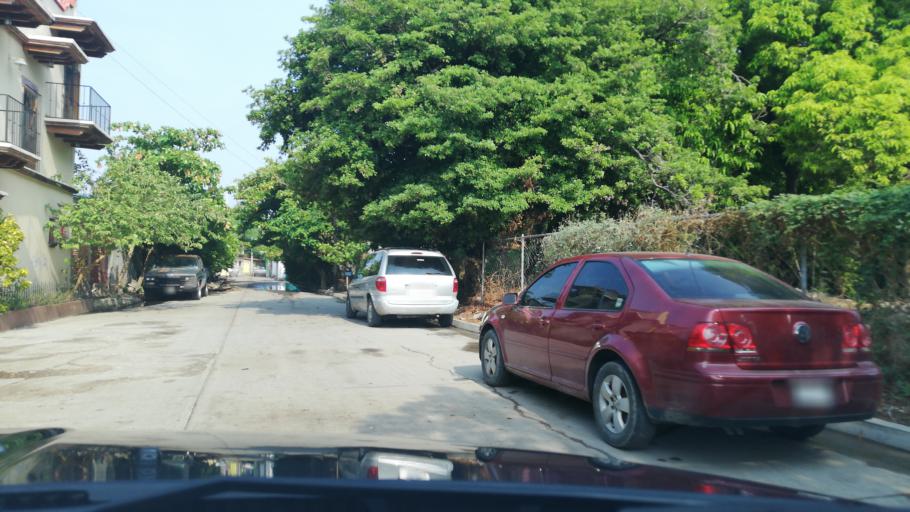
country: MX
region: Oaxaca
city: San Blas Atempa
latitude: 16.3368
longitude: -95.2280
